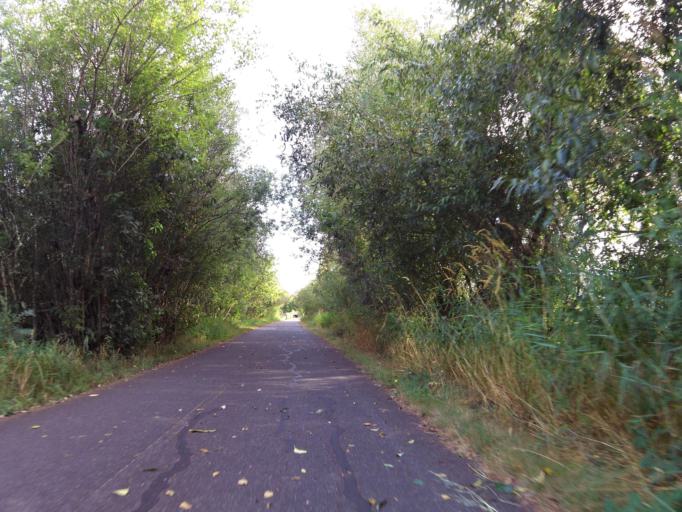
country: US
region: Washington
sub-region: Thurston County
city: Lacey
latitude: 47.0155
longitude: -122.8339
